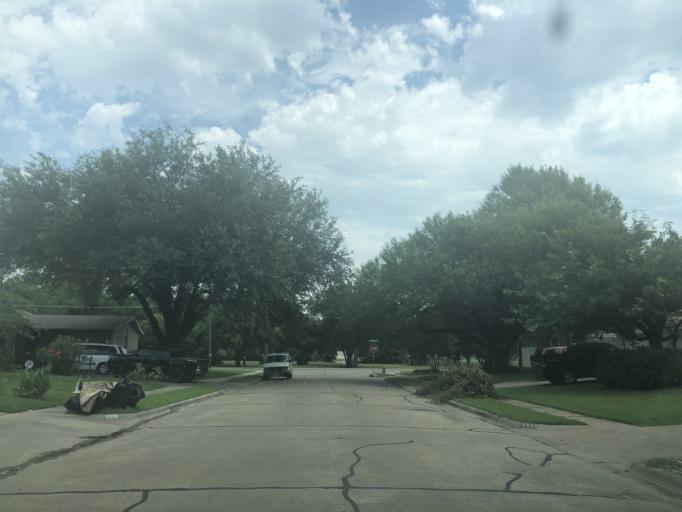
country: US
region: Texas
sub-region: Dallas County
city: Irving
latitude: 32.7932
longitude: -96.9372
